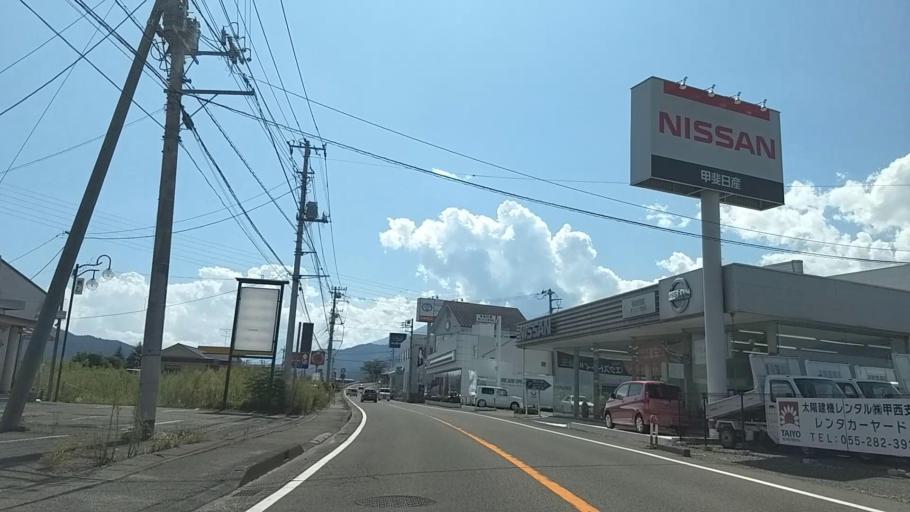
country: JP
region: Yamanashi
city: Ryuo
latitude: 35.5706
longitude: 138.4795
